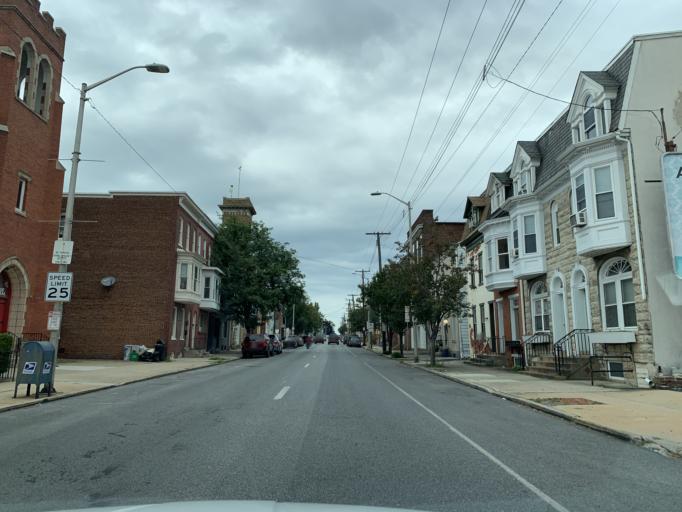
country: US
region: Pennsylvania
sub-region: York County
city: York
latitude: 39.9682
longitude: -76.7117
